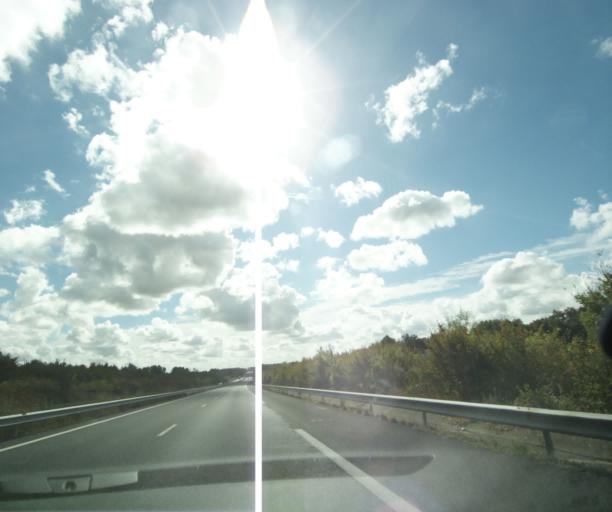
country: FR
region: Poitou-Charentes
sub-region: Departement de la Charente-Maritime
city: Bords
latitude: 45.8967
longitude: -0.7541
